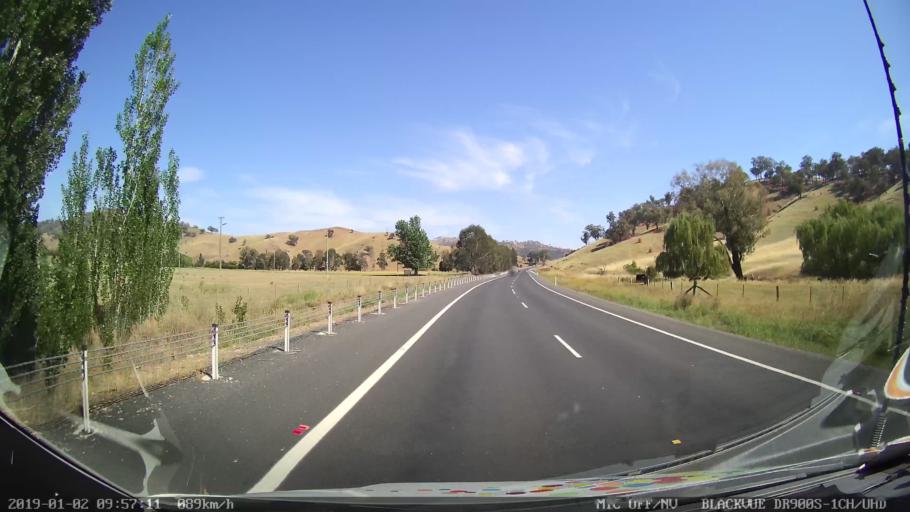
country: AU
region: New South Wales
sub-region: Tumut Shire
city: Tumut
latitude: -35.2086
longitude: 148.1679
